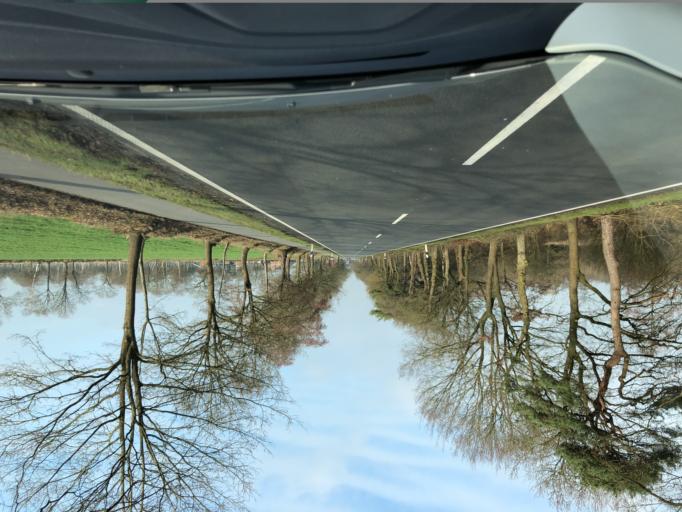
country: DE
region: Lower Saxony
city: Hesel
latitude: 53.3254
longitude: 7.6012
